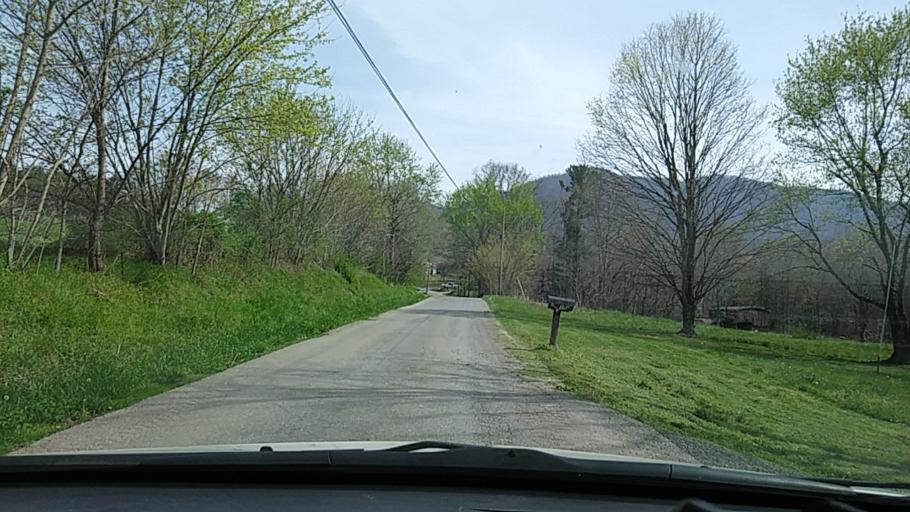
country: US
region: Tennessee
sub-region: Greene County
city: Tusculum
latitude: 36.0957
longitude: -82.7068
